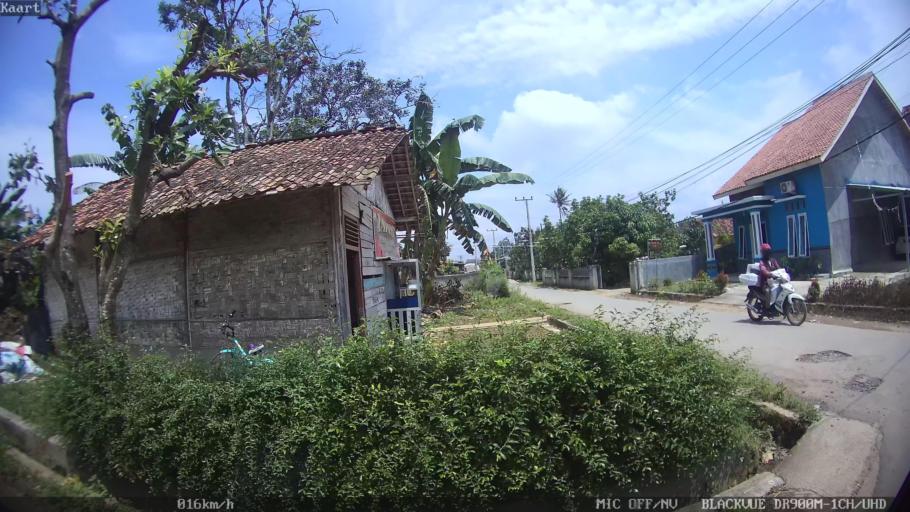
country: ID
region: Lampung
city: Kedaton
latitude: -5.3692
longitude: 105.3058
